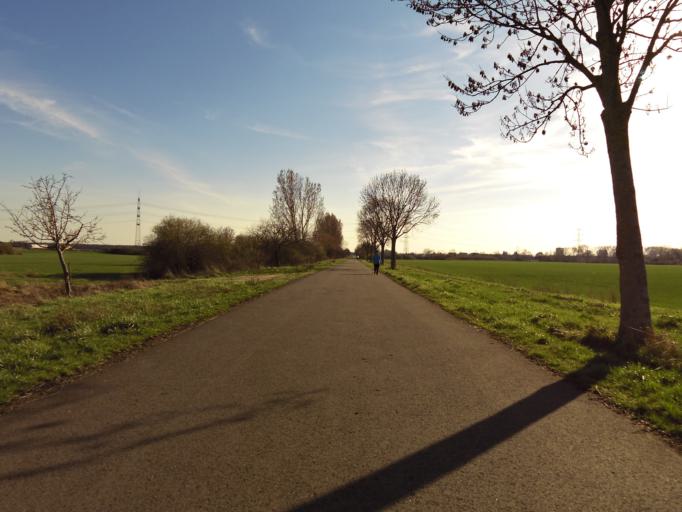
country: DE
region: Hesse
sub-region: Regierungsbezirk Darmstadt
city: Gross-Rohrheim
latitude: 49.7061
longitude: 8.4716
